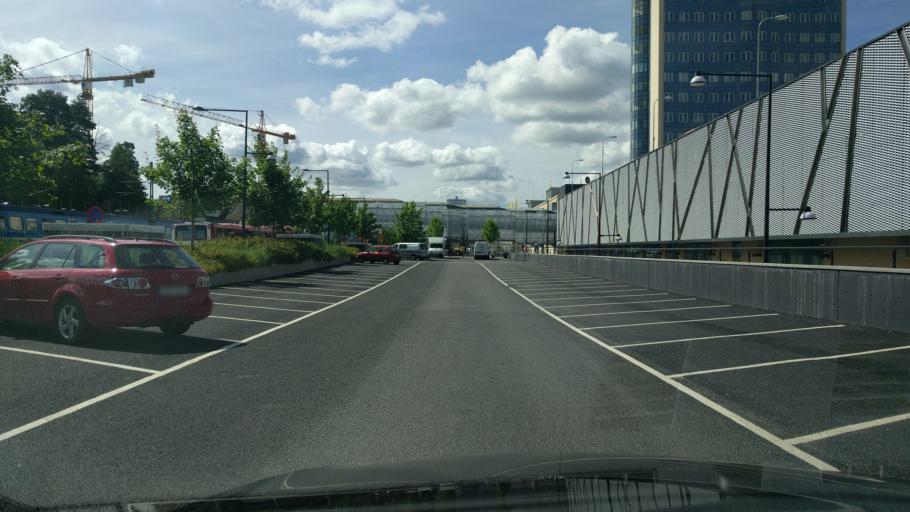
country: SE
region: Stockholm
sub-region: Taby Kommun
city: Taby
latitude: 59.4448
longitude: 18.0750
